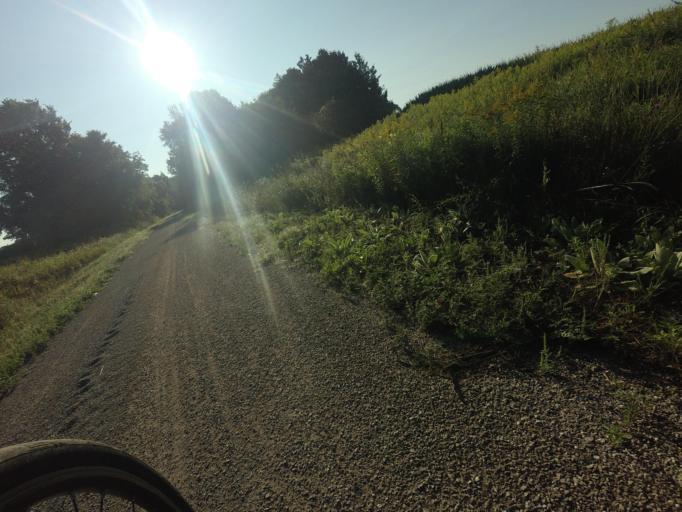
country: CA
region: Ontario
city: Goderich
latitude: 43.7643
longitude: -81.5329
